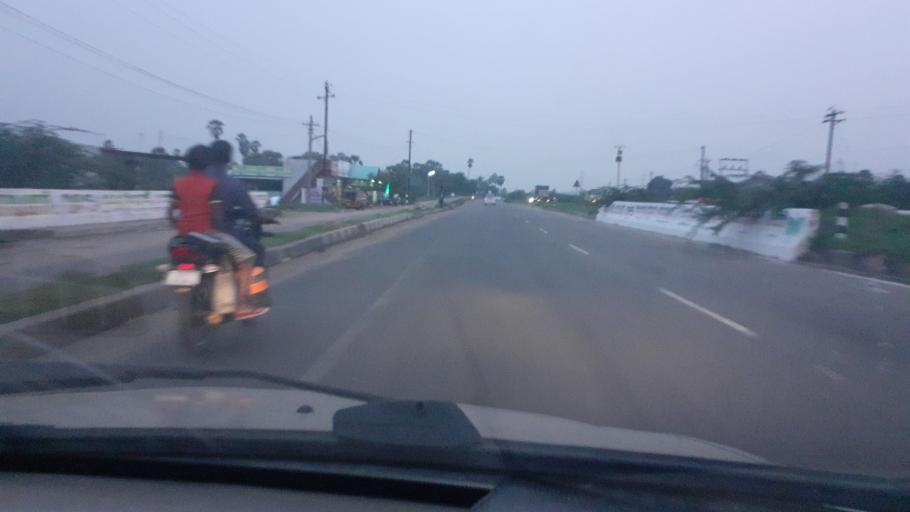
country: IN
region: Tamil Nadu
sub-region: Thoothukkudi
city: Srivaikuntam
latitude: 8.7103
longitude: 77.8220
